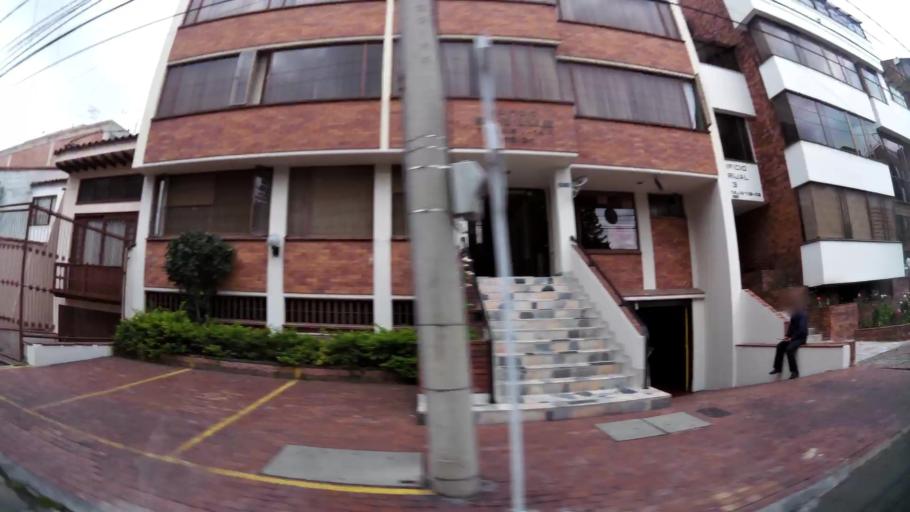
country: CO
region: Bogota D.C.
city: Barrio San Luis
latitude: 4.6993
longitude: -74.0414
